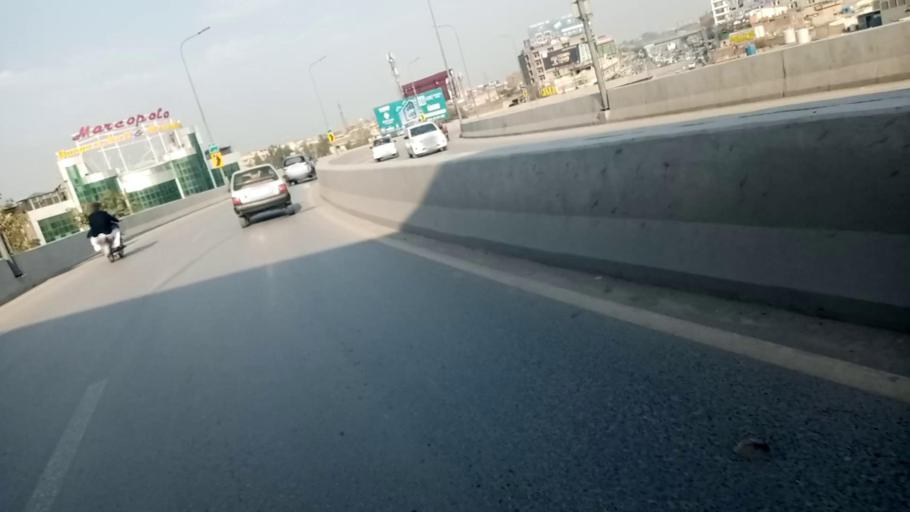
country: PK
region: Khyber Pakhtunkhwa
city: Peshawar
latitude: 33.9961
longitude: 71.4588
